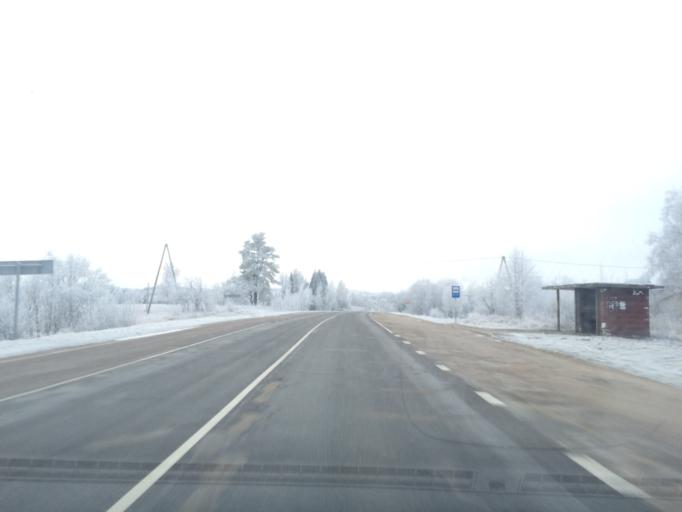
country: LV
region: Rezekne
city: Rezekne
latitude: 56.6155
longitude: 27.4487
